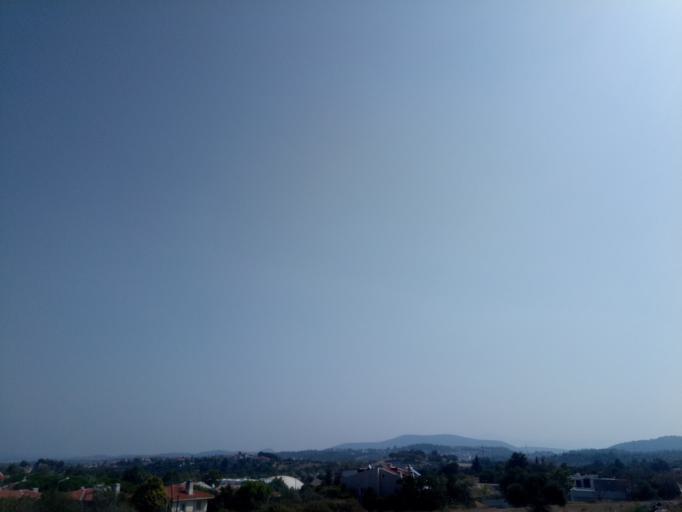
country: TR
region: Izmir
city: Urla
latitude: 38.3244
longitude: 26.7699
